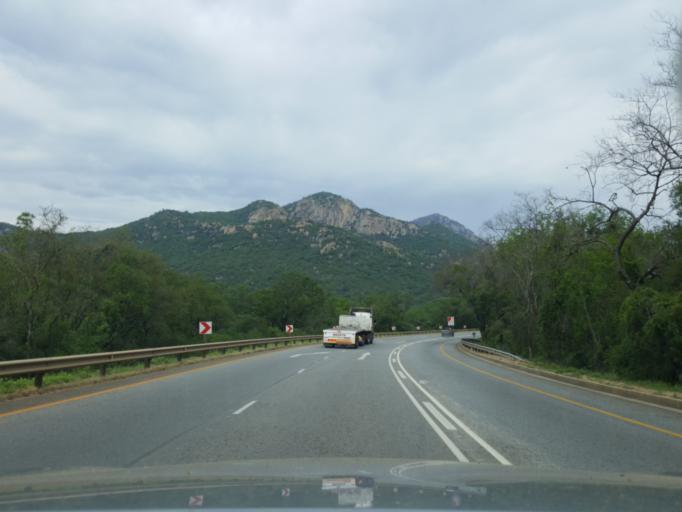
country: ZA
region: Mpumalanga
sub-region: Ehlanzeni District
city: Nelspruit
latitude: -25.5266
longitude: 31.2610
